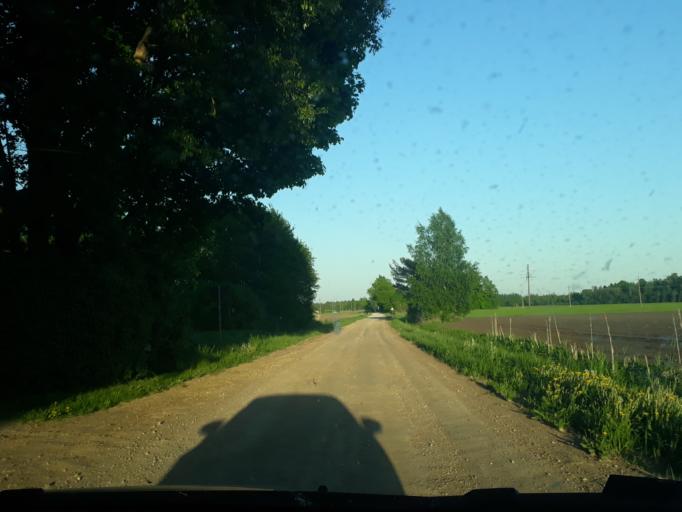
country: EE
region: Paernumaa
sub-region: Tootsi vald
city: Tootsi
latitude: 58.5852
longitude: 24.8991
